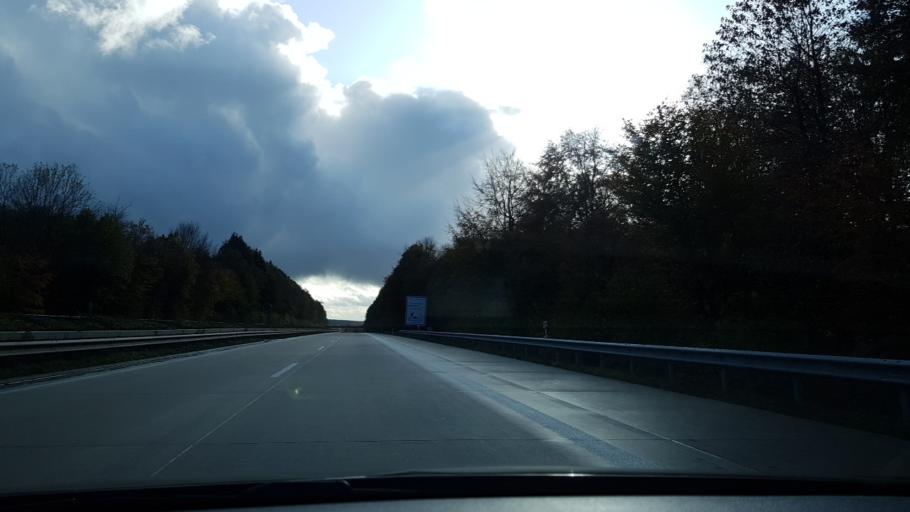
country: DE
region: Rheinland-Pfalz
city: Brockscheid
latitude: 50.1257
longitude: 6.8561
